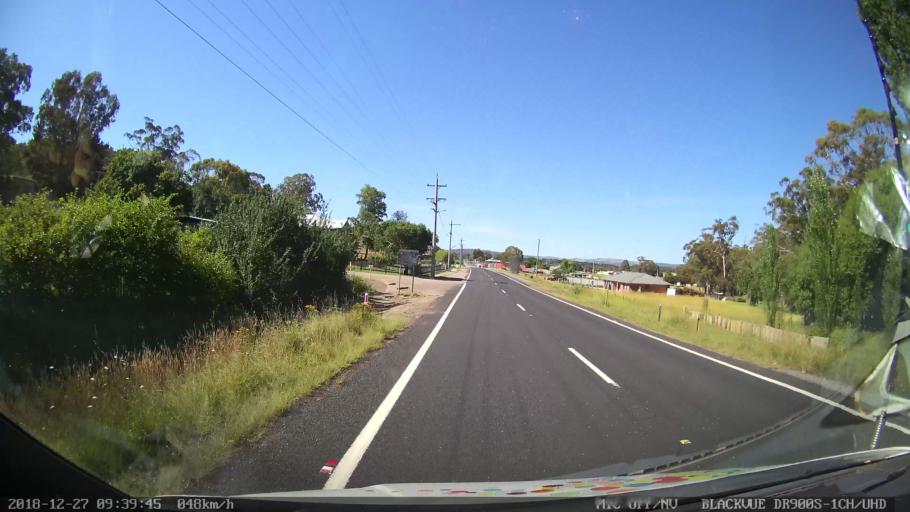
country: AU
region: New South Wales
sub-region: Lithgow
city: Portland
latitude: -33.2956
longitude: 150.0342
